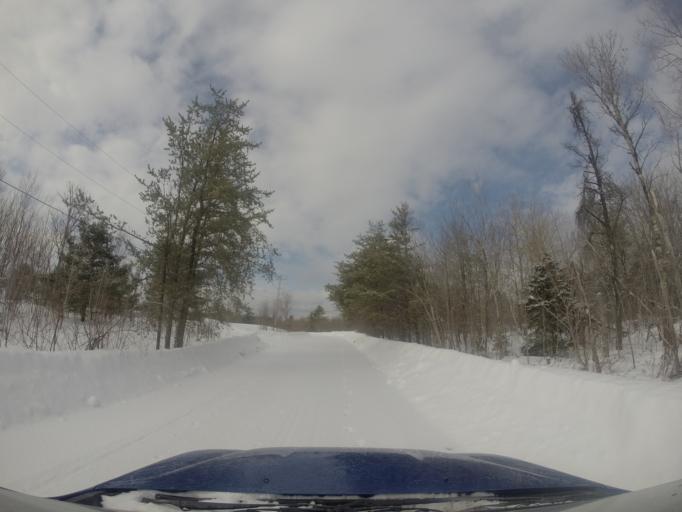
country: CA
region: Ontario
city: Greater Sudbury
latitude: 46.1046
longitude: -80.6778
